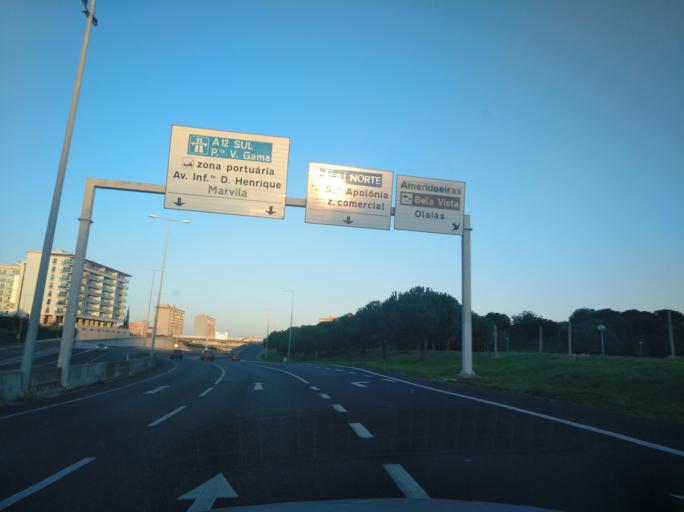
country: PT
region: Lisbon
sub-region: Lisbon
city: Lisbon
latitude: 38.7467
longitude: -9.1242
